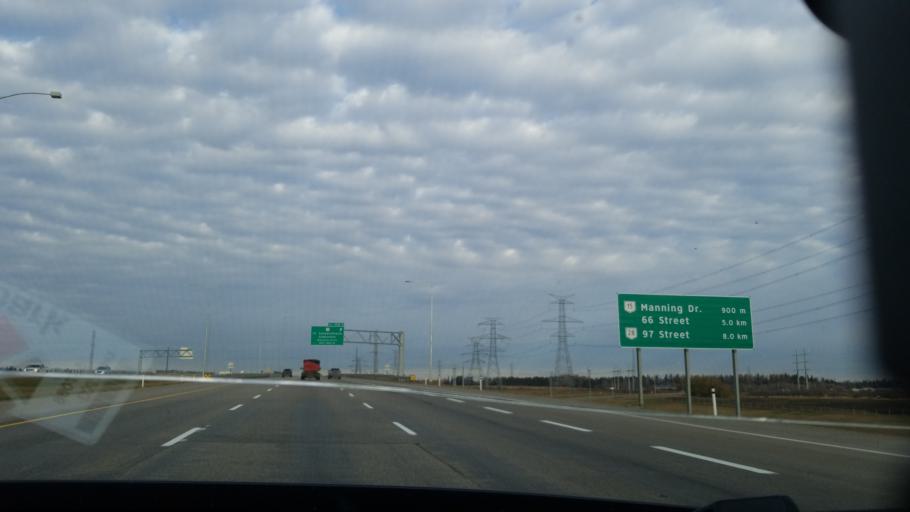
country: CA
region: Alberta
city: Sherwood Park
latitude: 53.6225
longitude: -113.3665
